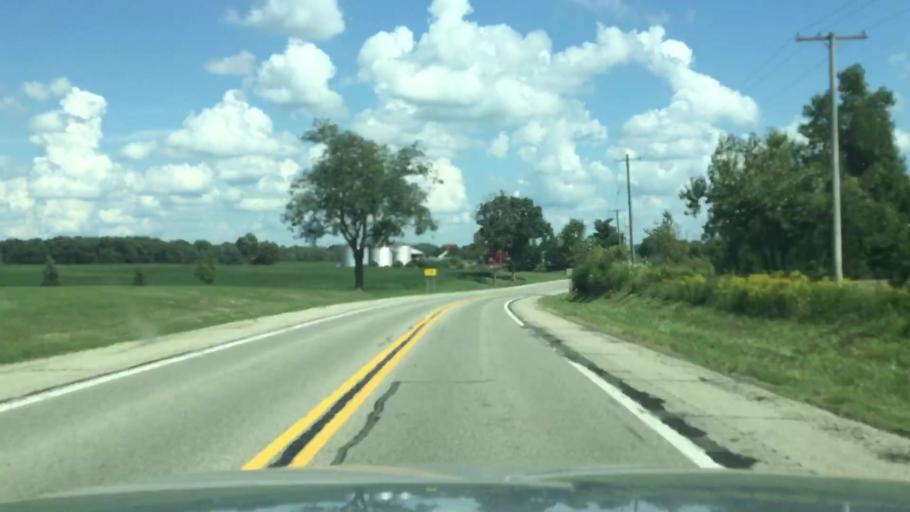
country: US
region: Michigan
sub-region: Lenawee County
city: Clinton
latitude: 42.0862
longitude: -83.9407
